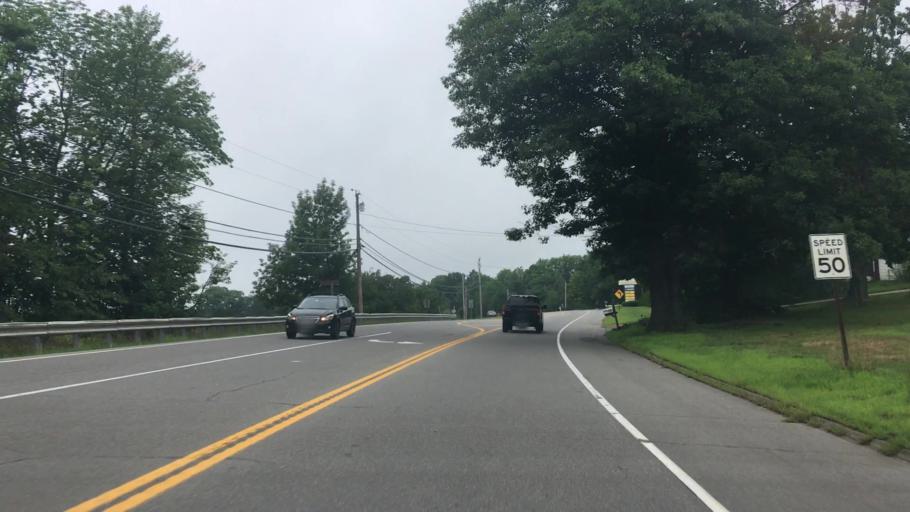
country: US
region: Maine
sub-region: York County
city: Lebanon
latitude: 43.4265
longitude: -70.8318
